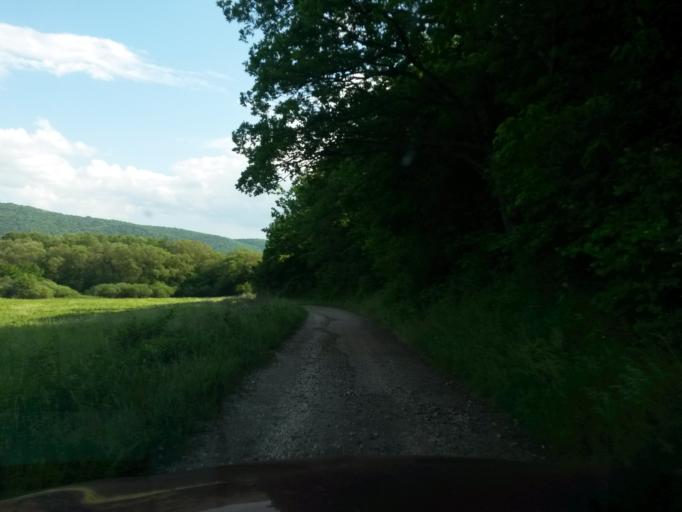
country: SK
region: Kosicky
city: Roznava
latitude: 48.5920
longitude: 20.6437
